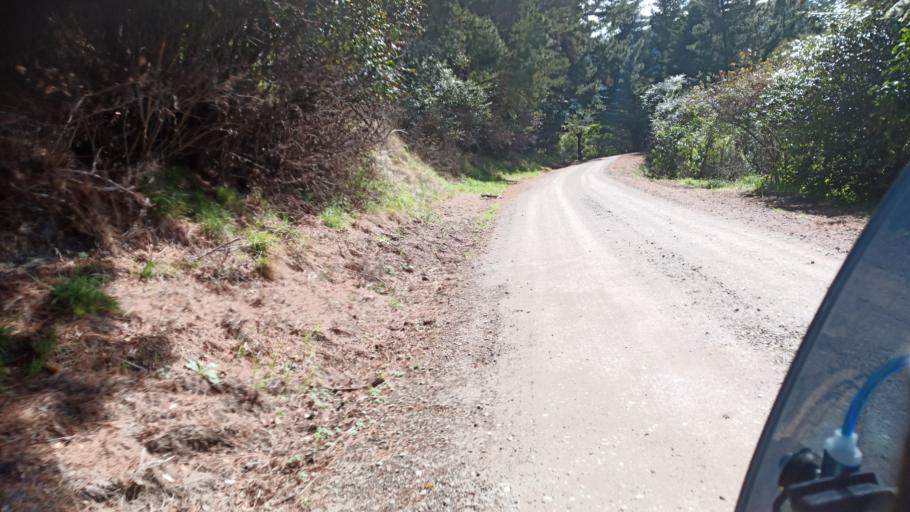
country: NZ
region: Hawke's Bay
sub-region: Wairoa District
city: Wairoa
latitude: -38.8144
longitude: 177.1555
